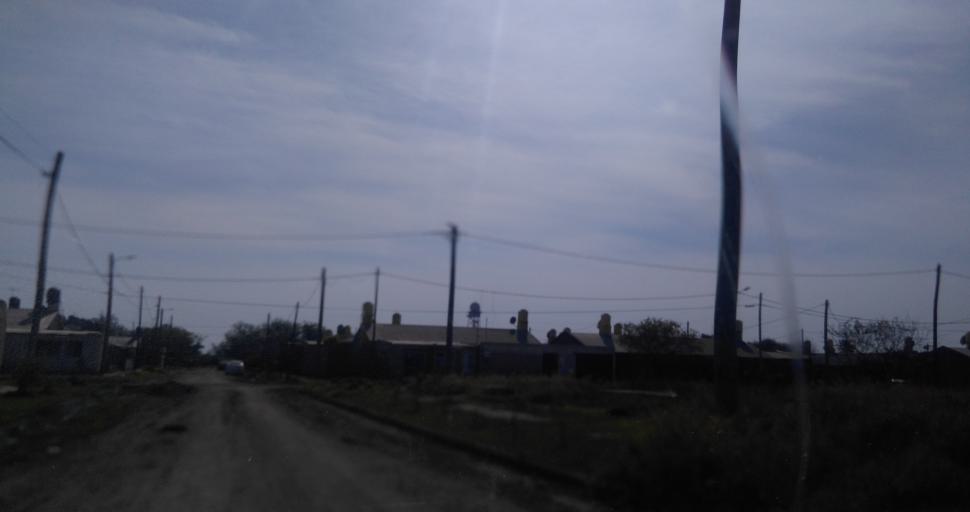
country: AR
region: Chaco
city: Fontana
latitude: -27.4559
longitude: -59.0486
